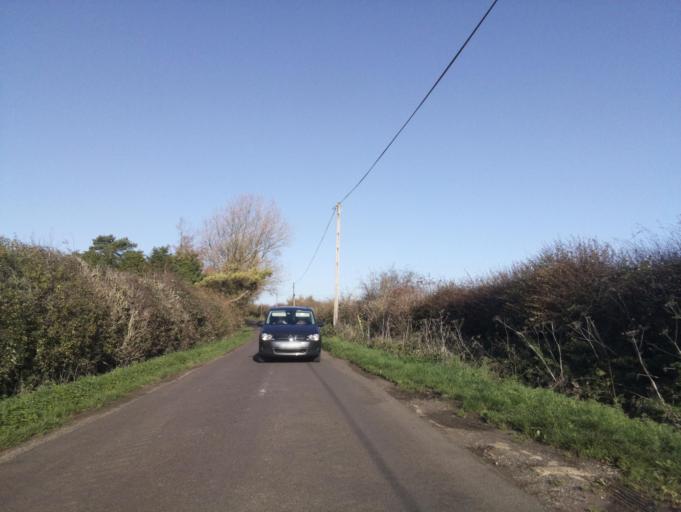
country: GB
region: England
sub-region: Dorset
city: Sherborne
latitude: 50.9993
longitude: -2.5119
